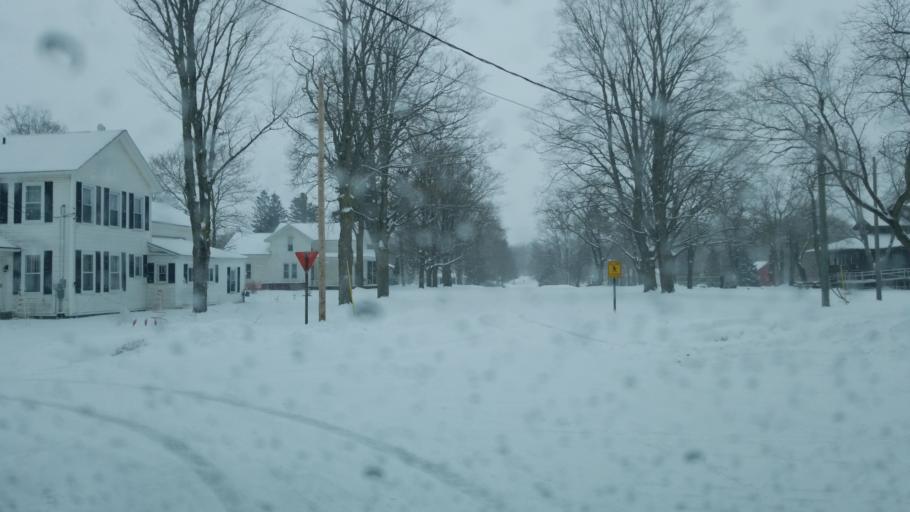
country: US
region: Michigan
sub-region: Osceola County
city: Reed City
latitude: 43.8501
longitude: -85.4460
